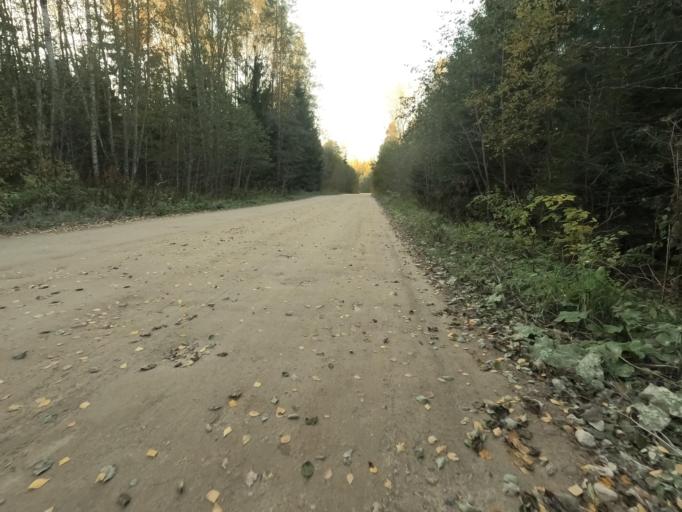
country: RU
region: Leningrad
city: Lyuban'
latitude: 59.0147
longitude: 31.0862
